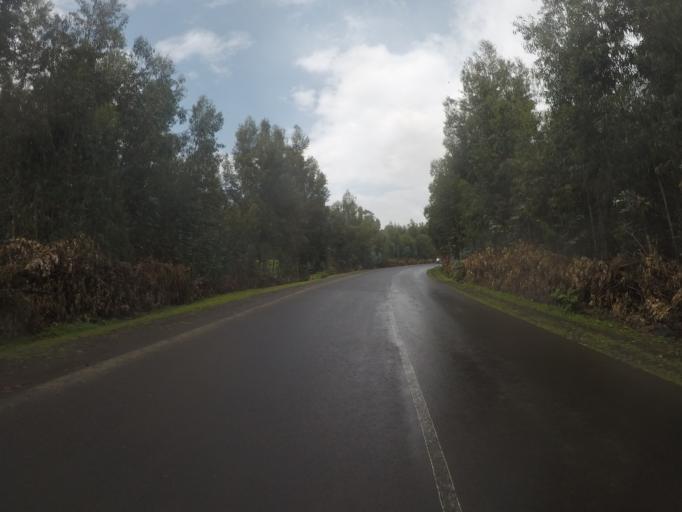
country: ET
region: Amhara
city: Debark'
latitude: 13.1164
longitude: 37.8716
